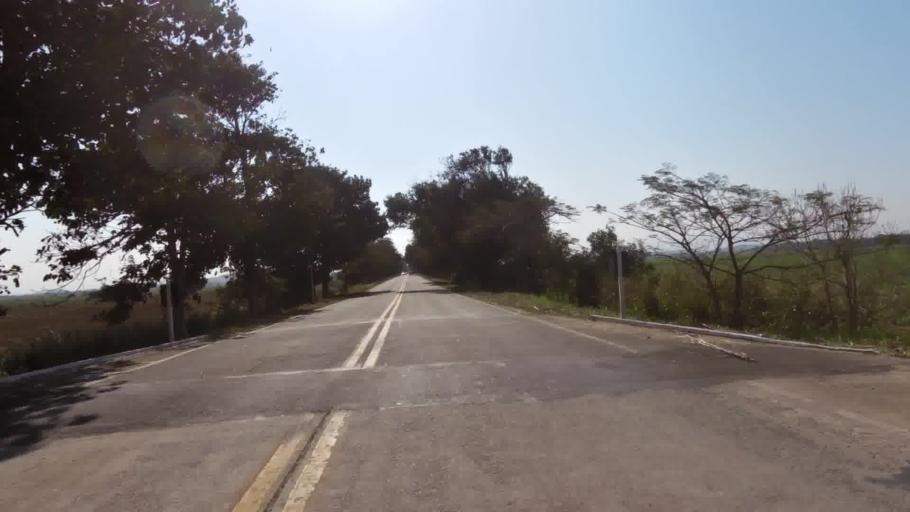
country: BR
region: Espirito Santo
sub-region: Itapemirim
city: Itapemirim
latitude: -21.0000
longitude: -40.8442
